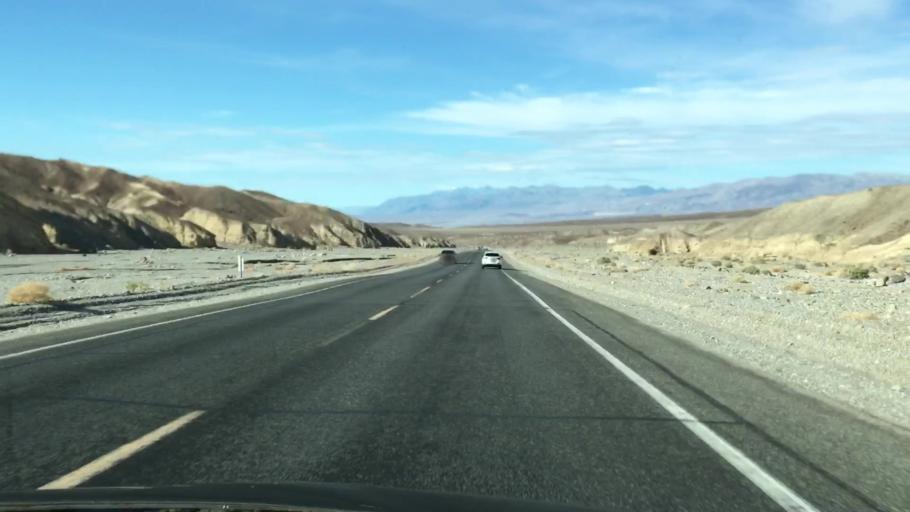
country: US
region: Nevada
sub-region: Nye County
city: Beatty
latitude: 36.4236
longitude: -116.8107
